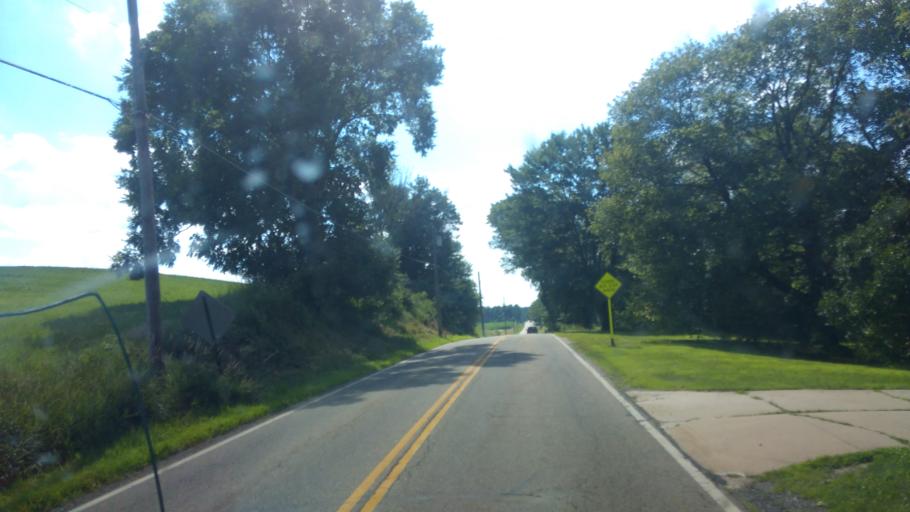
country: US
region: Ohio
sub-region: Stark County
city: Richville
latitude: 40.7309
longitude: -81.4705
